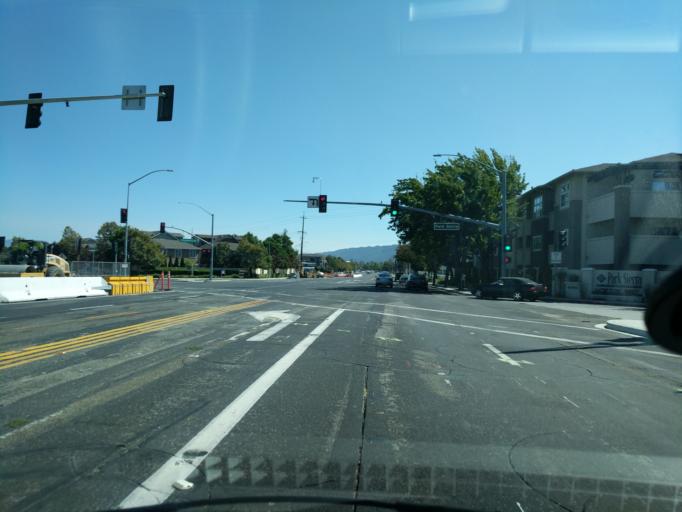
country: US
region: California
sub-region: Alameda County
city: Dublin
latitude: 37.7112
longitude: -121.9104
